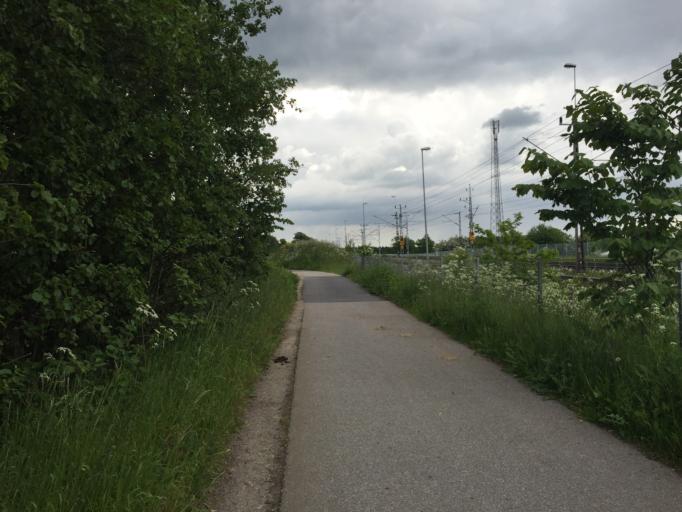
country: SE
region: Skane
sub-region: Lunds Kommun
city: Lund
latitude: 55.7405
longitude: 13.1921
